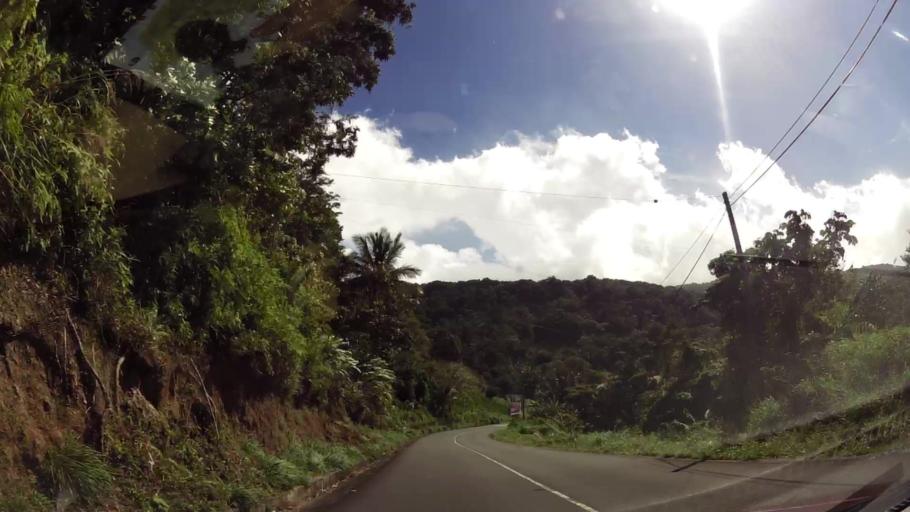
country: DM
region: Saint Paul
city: Pont Casse
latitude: 15.3618
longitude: -61.3553
